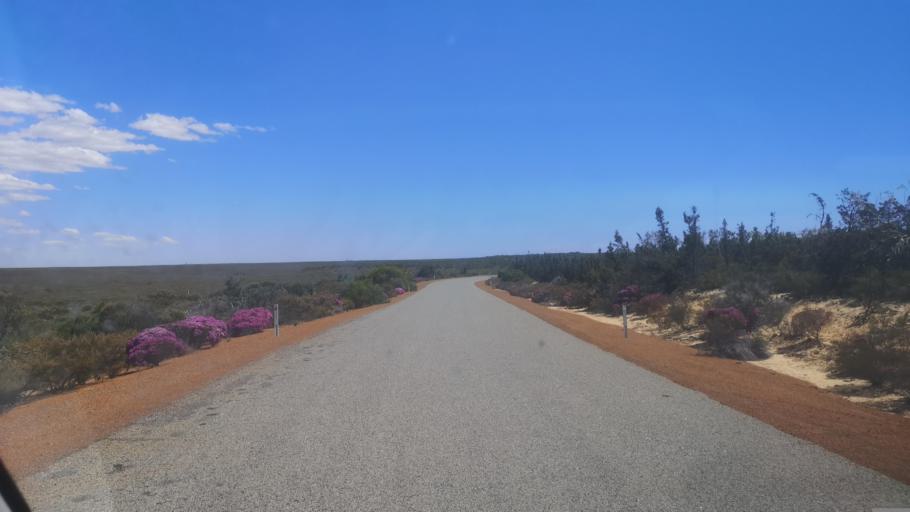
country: AU
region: Western Australia
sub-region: Northampton Shire
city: Kalbarri
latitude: -27.8149
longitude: 114.4661
